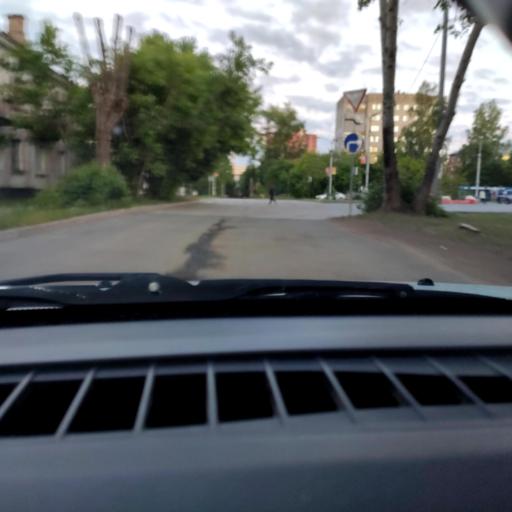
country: RU
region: Perm
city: Perm
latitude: 58.1141
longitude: 56.3092
